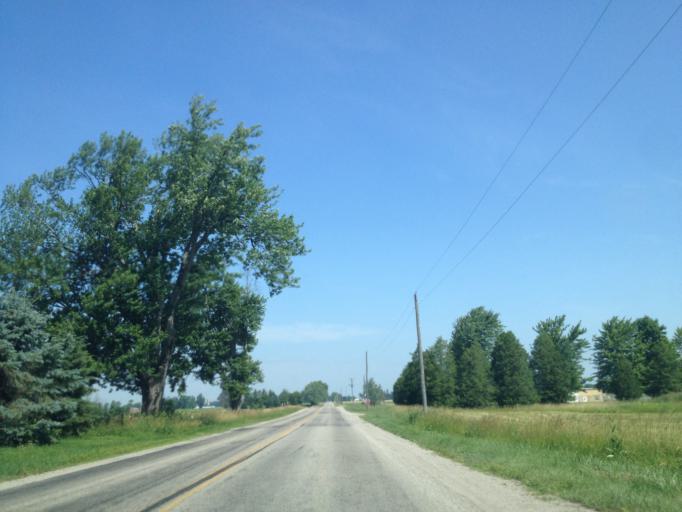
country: CA
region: Ontario
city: London
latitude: 43.1423
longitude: -81.2136
